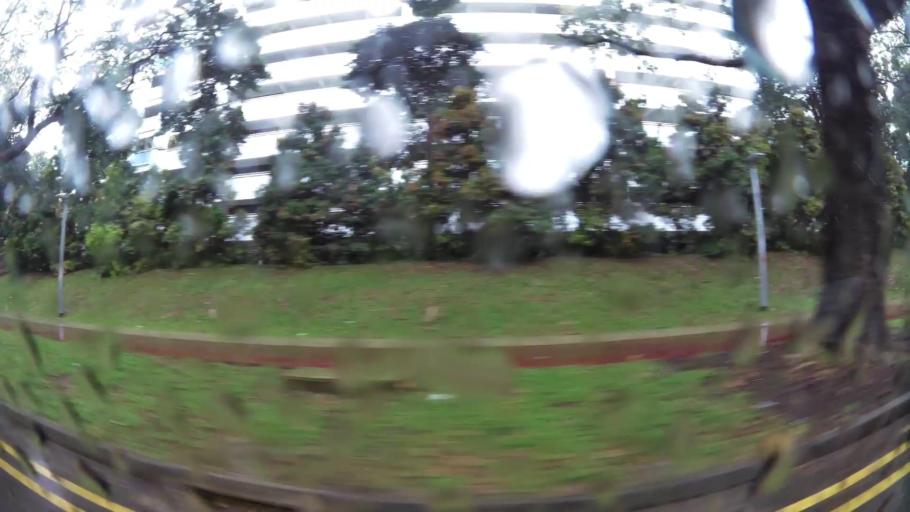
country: SG
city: Singapore
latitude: 1.3640
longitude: 103.8469
